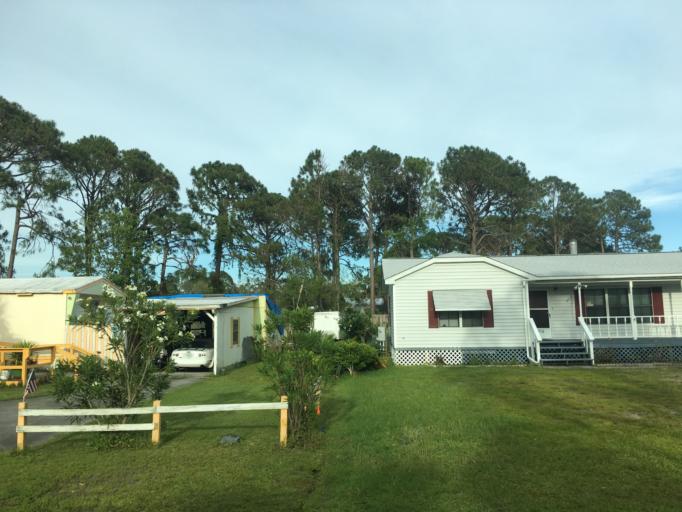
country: US
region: Florida
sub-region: Bay County
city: Upper Grand Lagoon
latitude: 30.1662
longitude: -85.7645
